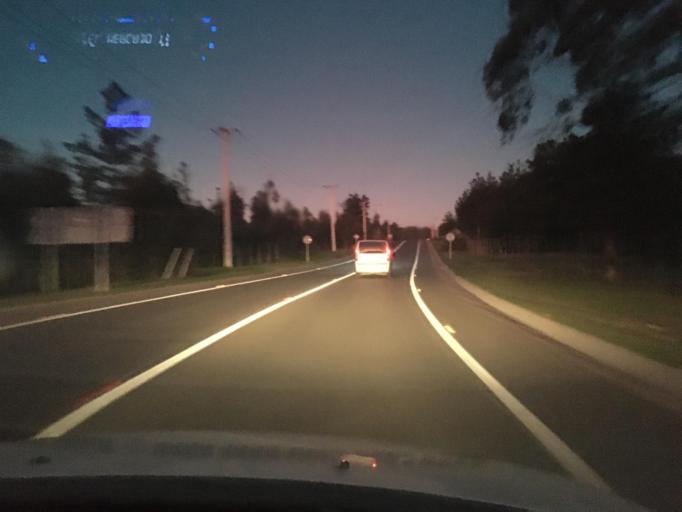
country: CL
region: Valparaiso
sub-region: San Antonio Province
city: El Tabo
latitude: -33.4225
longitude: -71.6791
